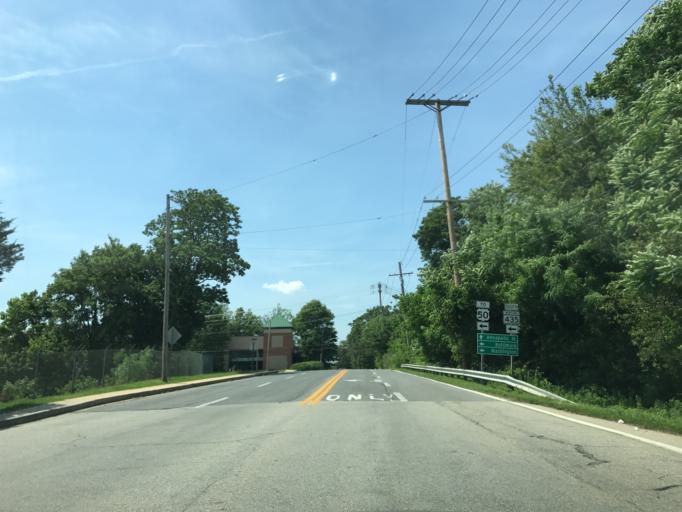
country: US
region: Maryland
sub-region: Anne Arundel County
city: Naval Academy
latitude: 38.9882
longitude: -76.4998
